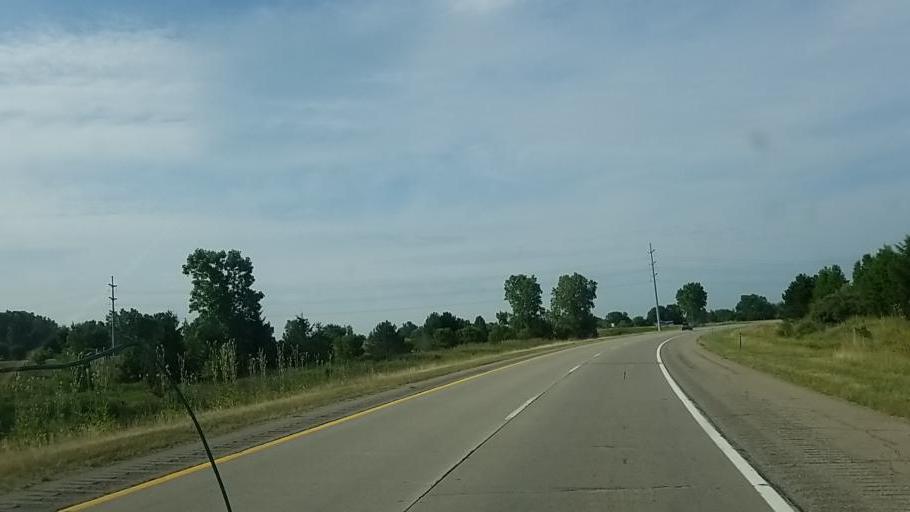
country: US
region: Michigan
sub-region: Eaton County
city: Dimondale
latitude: 42.6906
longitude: -84.6692
